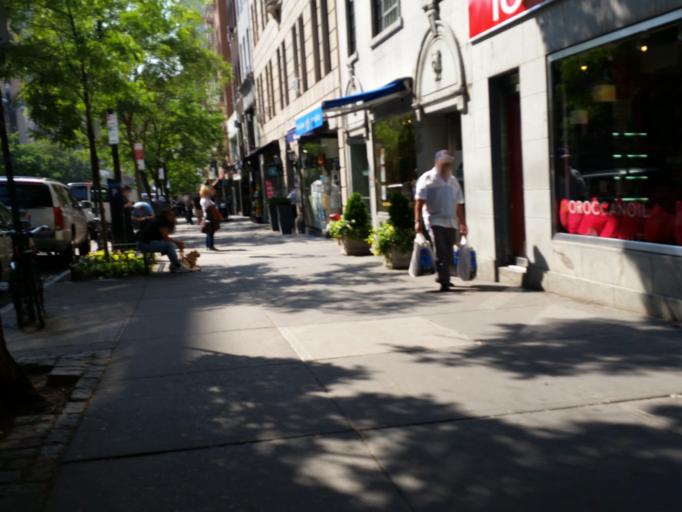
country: US
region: New York
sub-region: New York County
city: Manhattan
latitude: 40.7776
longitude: -73.9793
